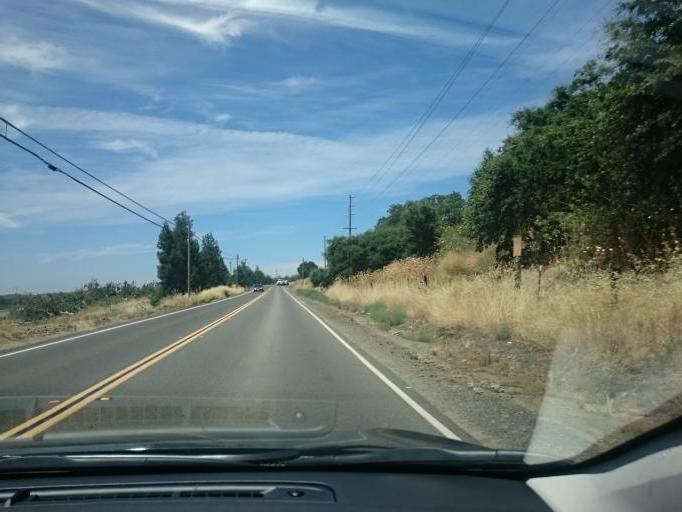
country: US
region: California
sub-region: Stanislaus County
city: Waterford
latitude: 37.6421
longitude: -120.6413
